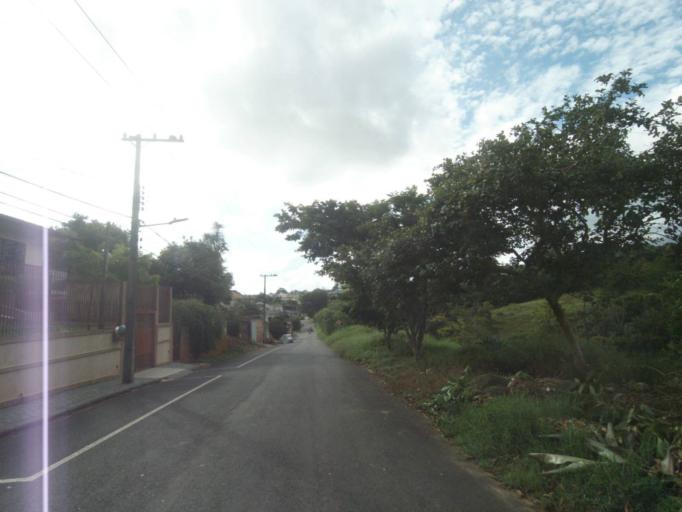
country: BR
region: Parana
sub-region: Telemaco Borba
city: Telemaco Borba
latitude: -24.3360
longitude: -50.6100
